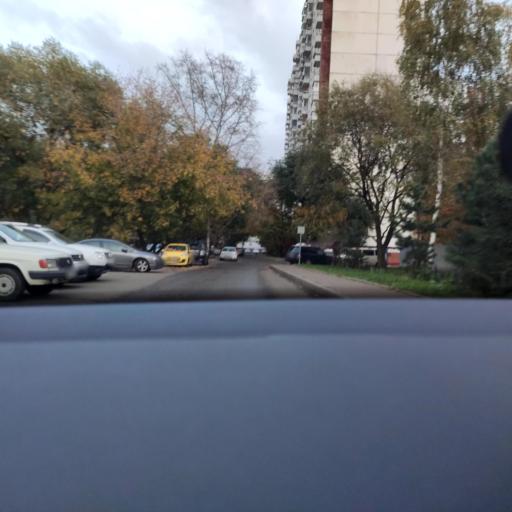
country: RU
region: Moscow
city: Orekhovo-Borisovo
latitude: 55.6299
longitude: 37.7377
